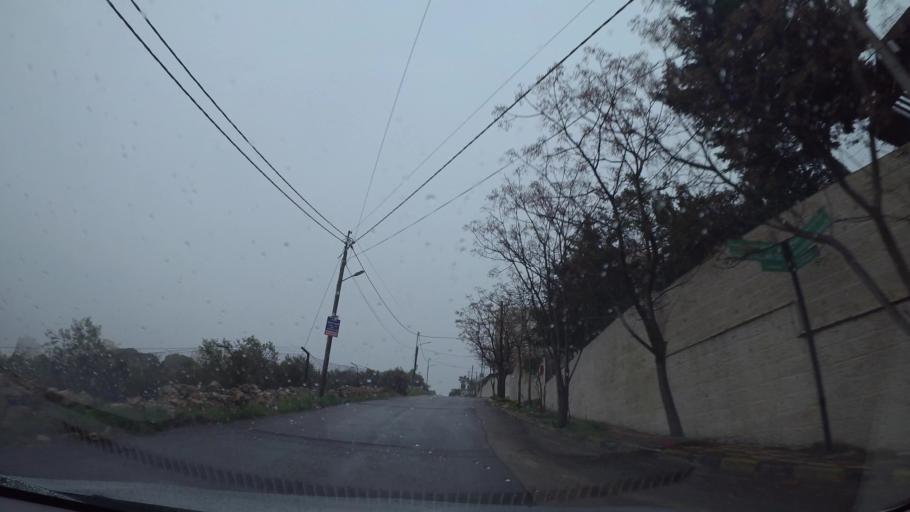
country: JO
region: Amman
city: Al Jubayhah
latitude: 32.0326
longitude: 35.8523
